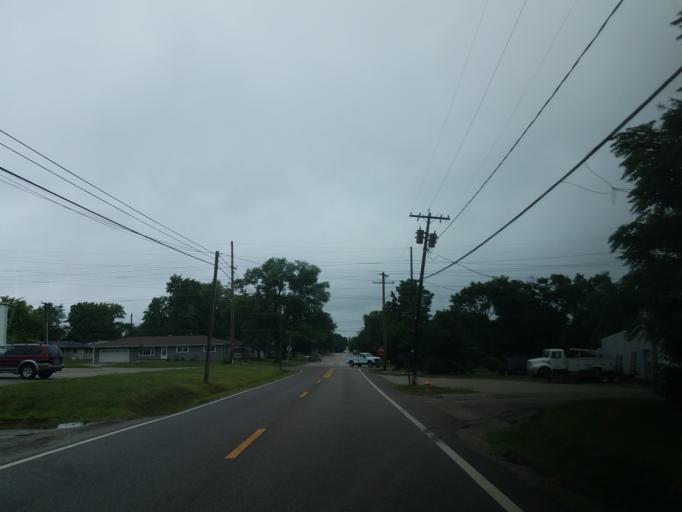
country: US
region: Illinois
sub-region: McLean County
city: Bloomington
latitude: 40.4629
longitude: -88.9816
